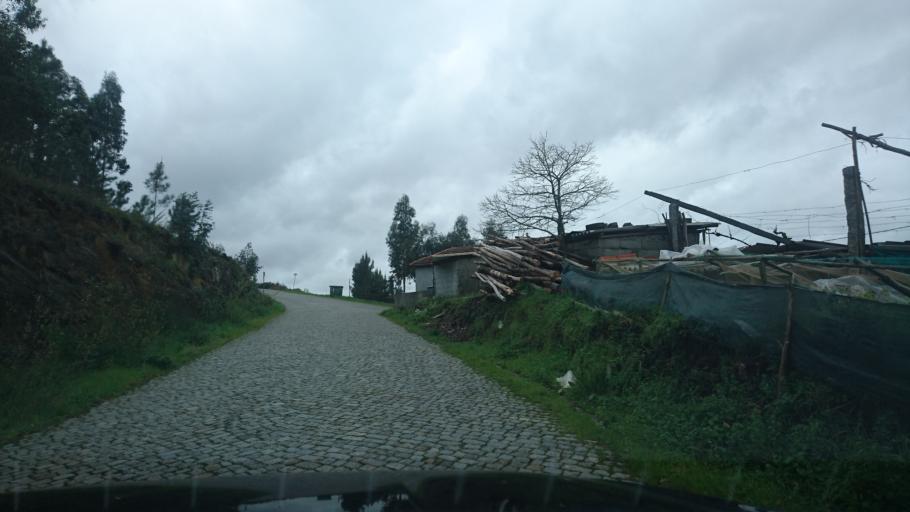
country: PT
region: Porto
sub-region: Paredes
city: Recarei
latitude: 41.1382
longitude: -8.3970
